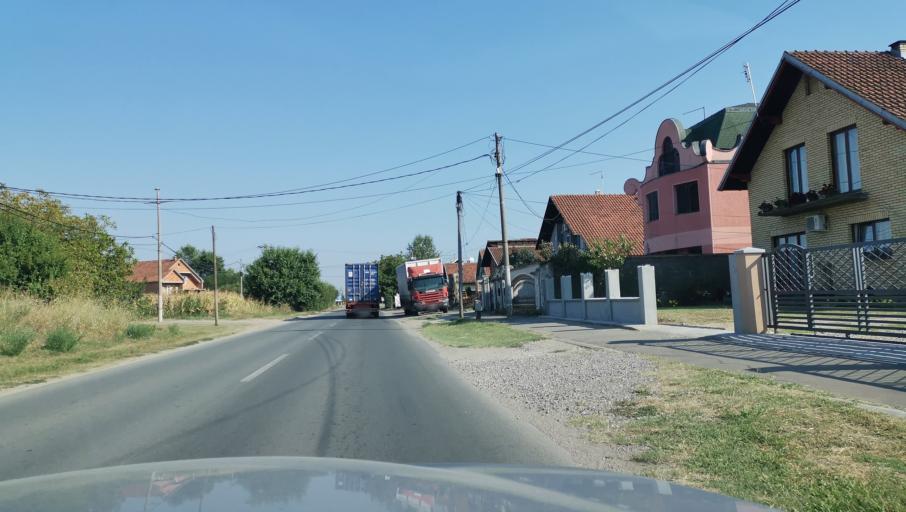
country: RS
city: Dobanovci
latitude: 44.8147
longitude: 20.2375
